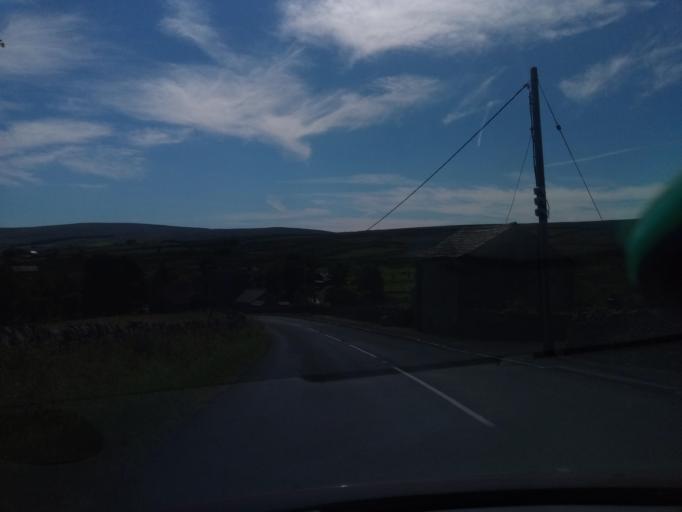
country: GB
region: England
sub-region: County Durham
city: Holwick
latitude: 54.7688
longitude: -2.2437
